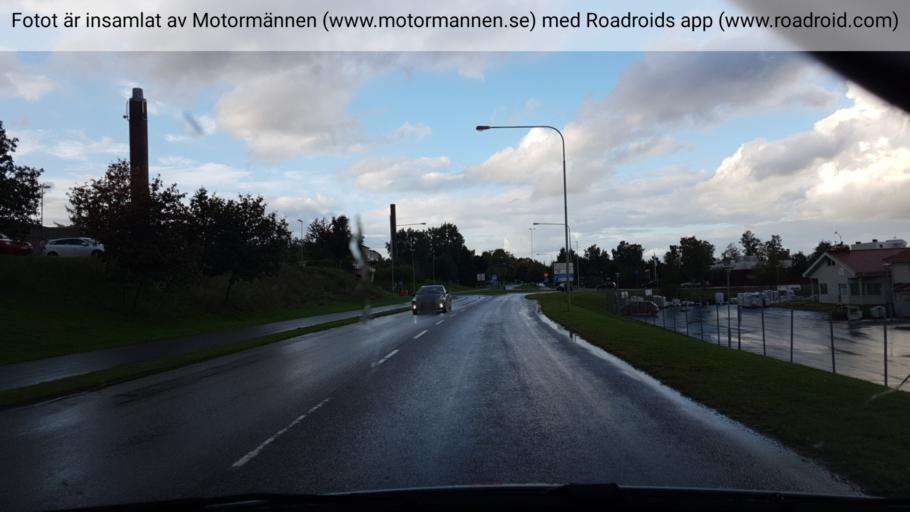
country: SE
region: Vaestra Goetaland
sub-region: Skovde Kommun
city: Skoevde
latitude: 58.4056
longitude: 13.8662
